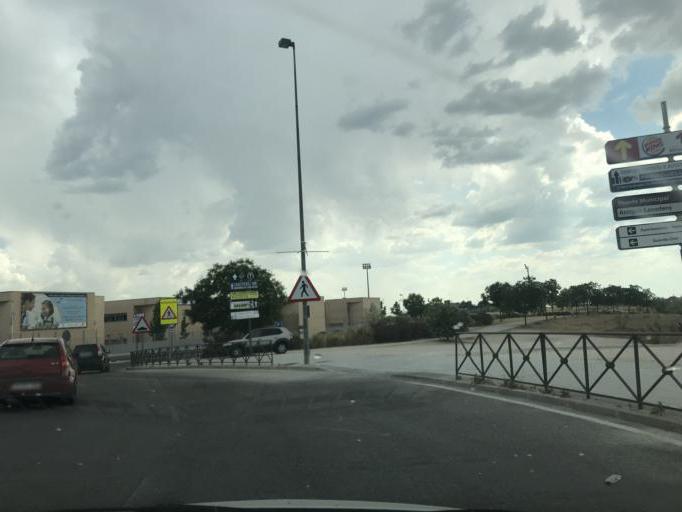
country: ES
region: Madrid
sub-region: Provincia de Madrid
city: Paracuellos de Jarama
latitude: 40.5061
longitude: -3.5197
